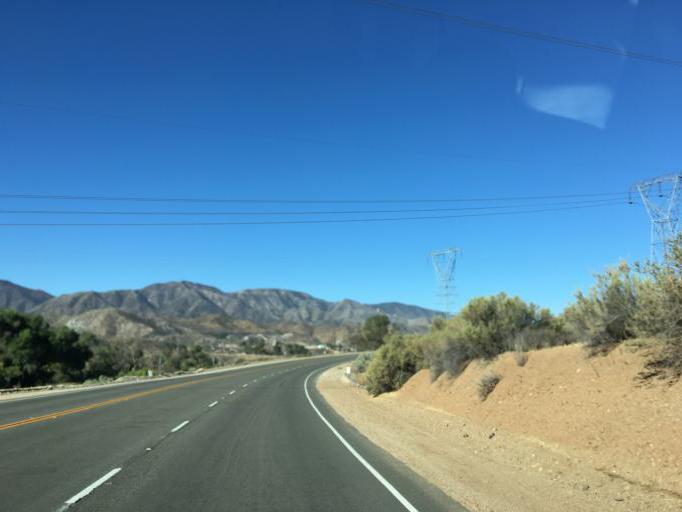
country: US
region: California
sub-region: Los Angeles County
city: Acton
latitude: 34.4397
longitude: -118.2169
